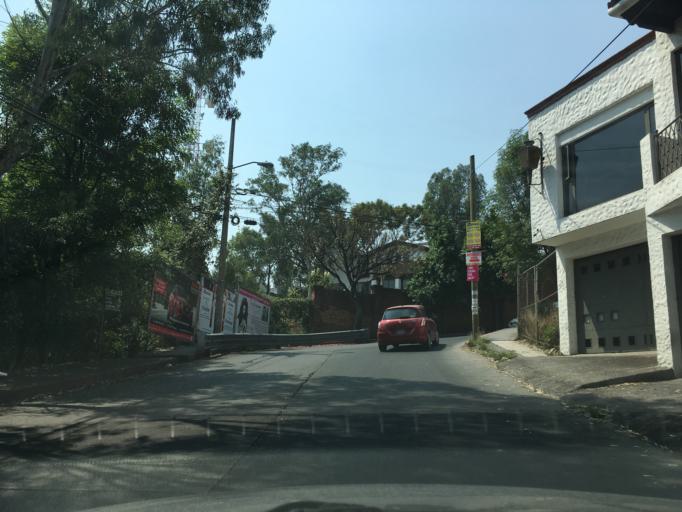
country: MX
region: Michoacan
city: Morelia
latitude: 19.6779
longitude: -101.1859
